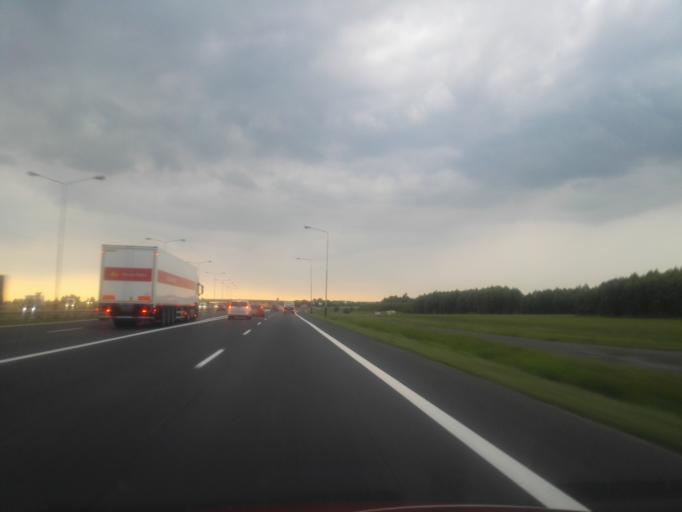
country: PL
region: Lodz Voivodeship
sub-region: Piotrkow Trybunalski
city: Piotrkow Trybunalski
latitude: 51.4314
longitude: 19.6417
